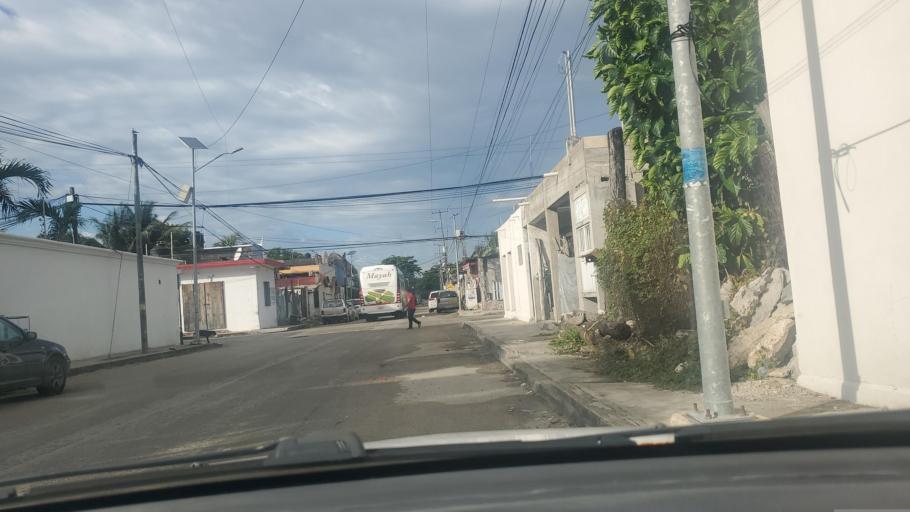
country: MX
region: Quintana Roo
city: Tulum
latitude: 20.2133
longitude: -87.4609
